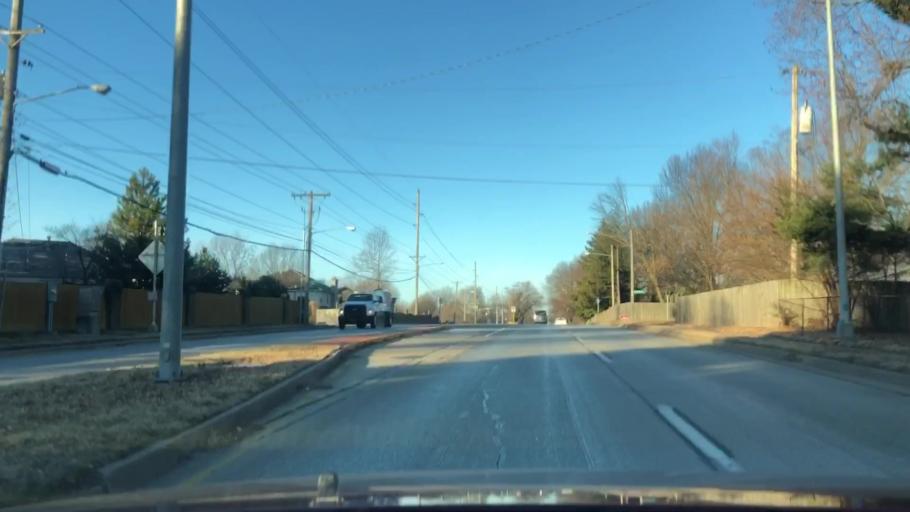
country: US
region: Missouri
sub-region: Greene County
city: Springfield
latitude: 37.1587
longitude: -93.2455
